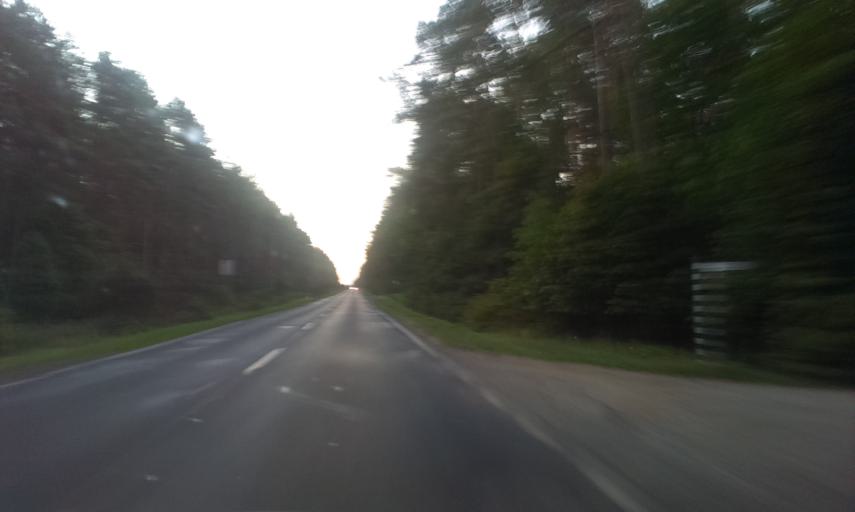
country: PL
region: Kujawsko-Pomorskie
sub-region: Powiat tucholski
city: Tuchola
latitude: 53.5469
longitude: 17.9289
